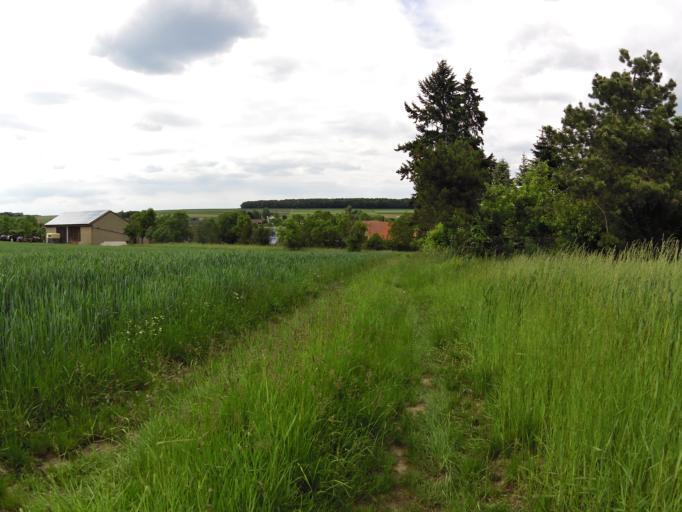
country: DE
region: Bavaria
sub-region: Regierungsbezirk Unterfranken
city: Theilheim
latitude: 49.7313
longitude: 10.0364
